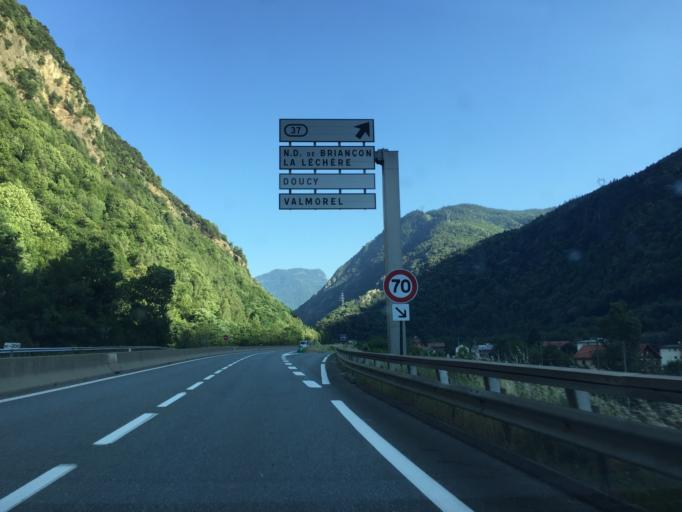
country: FR
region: Rhone-Alpes
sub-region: Departement de la Savoie
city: Aigueblanche
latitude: 45.5430
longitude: 6.4683
